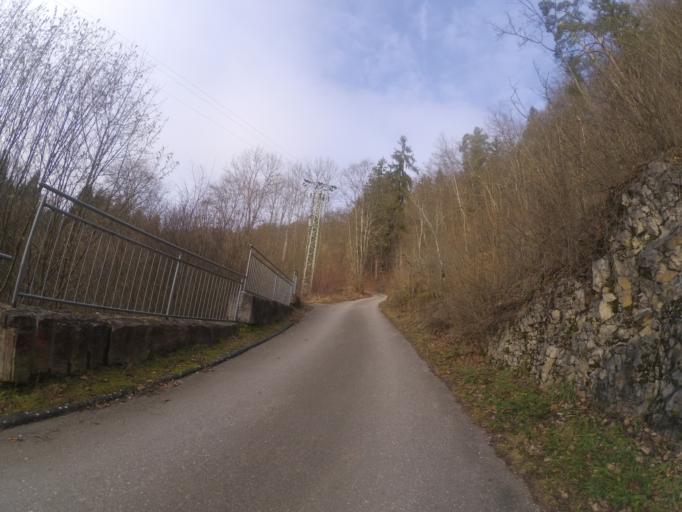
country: DE
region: Baden-Wuerttemberg
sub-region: Tuebingen Region
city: Lauterach
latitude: 48.2612
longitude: 9.5627
